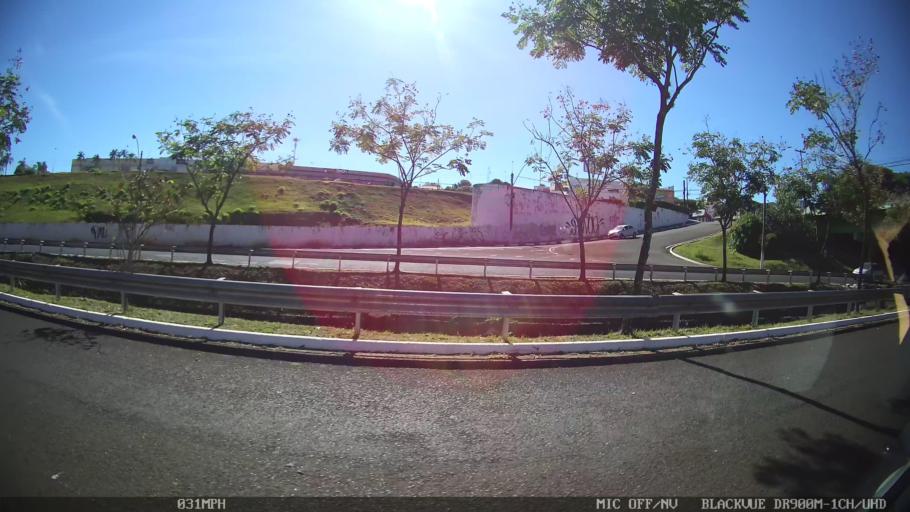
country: BR
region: Sao Paulo
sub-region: Franca
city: Franca
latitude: -20.5205
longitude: -47.3841
